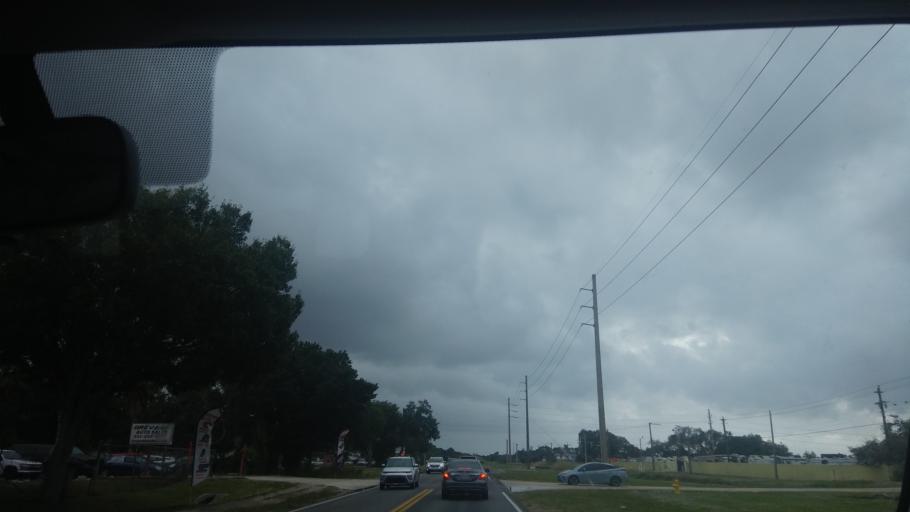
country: US
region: Florida
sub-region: Brevard County
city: Palm Bay
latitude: 27.9937
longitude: -80.6219
